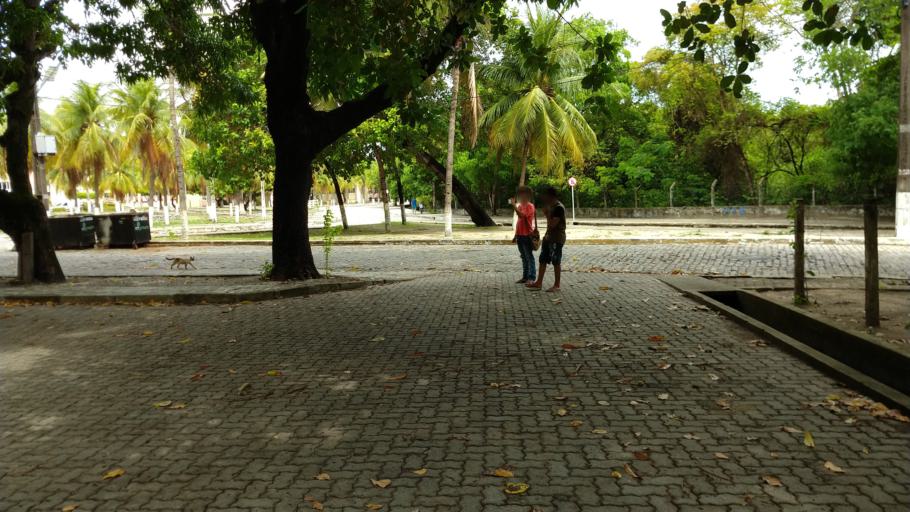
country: BR
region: Ceara
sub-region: Fortaleza
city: Fortaleza
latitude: -3.7446
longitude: -38.5742
